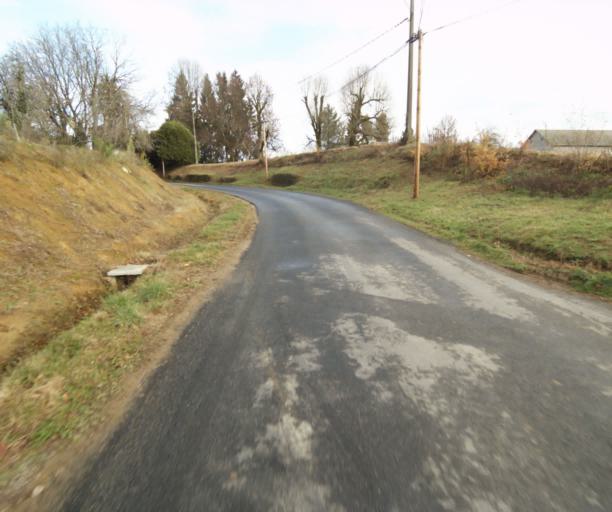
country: FR
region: Limousin
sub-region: Departement de la Correze
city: Saint-Mexant
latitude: 45.2767
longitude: 1.6066
